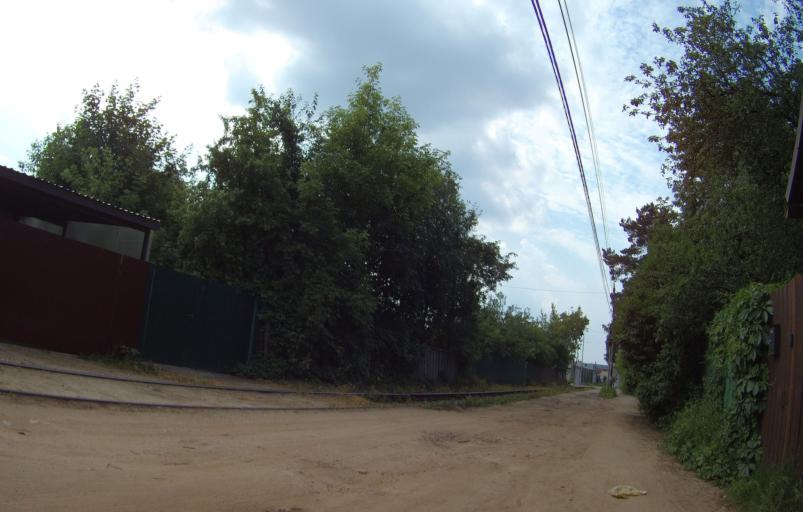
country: RU
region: Moskovskaya
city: Bykovo
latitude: 55.6223
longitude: 38.0680
